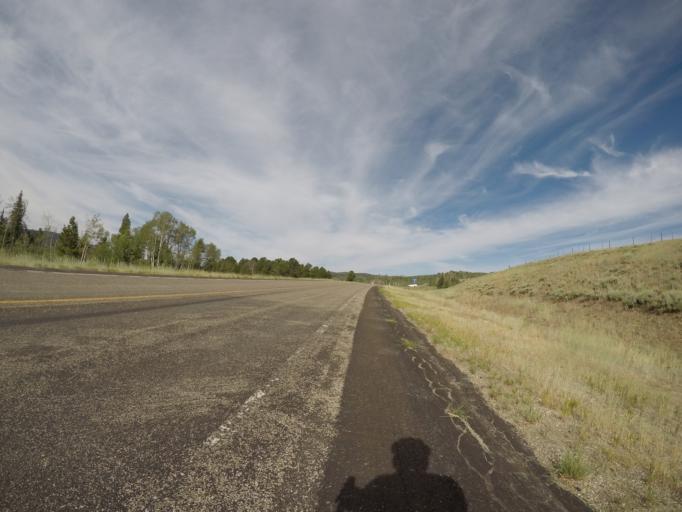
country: US
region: Wyoming
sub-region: Carbon County
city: Saratoga
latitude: 41.1774
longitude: -106.8849
